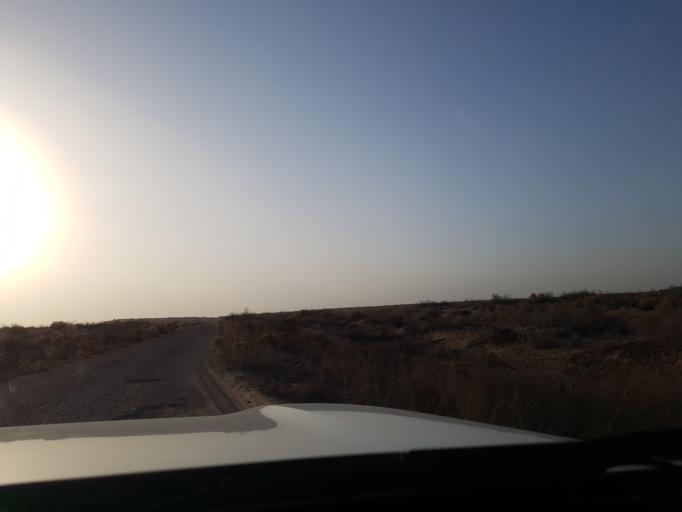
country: UZ
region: Xorazm
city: Khiwa
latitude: 41.1535
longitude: 60.6714
